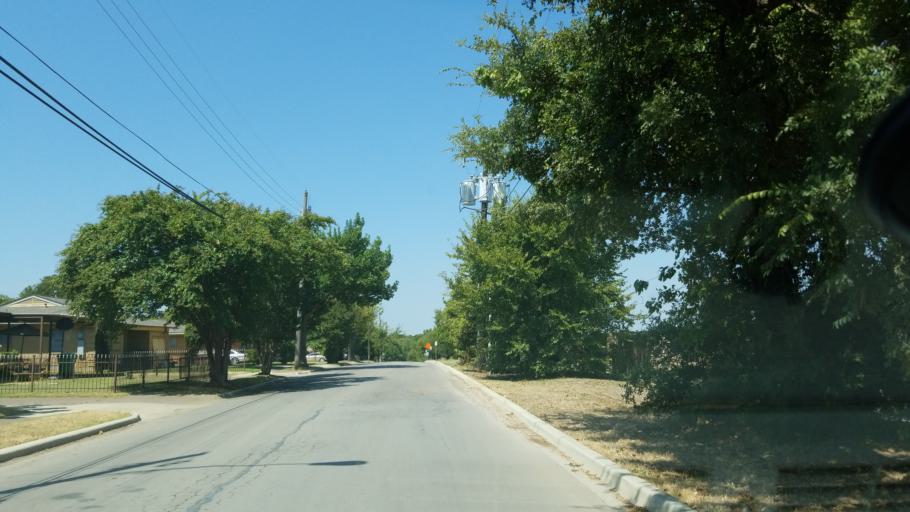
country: US
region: Texas
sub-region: Dallas County
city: Cockrell Hill
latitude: 32.7351
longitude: -96.8930
